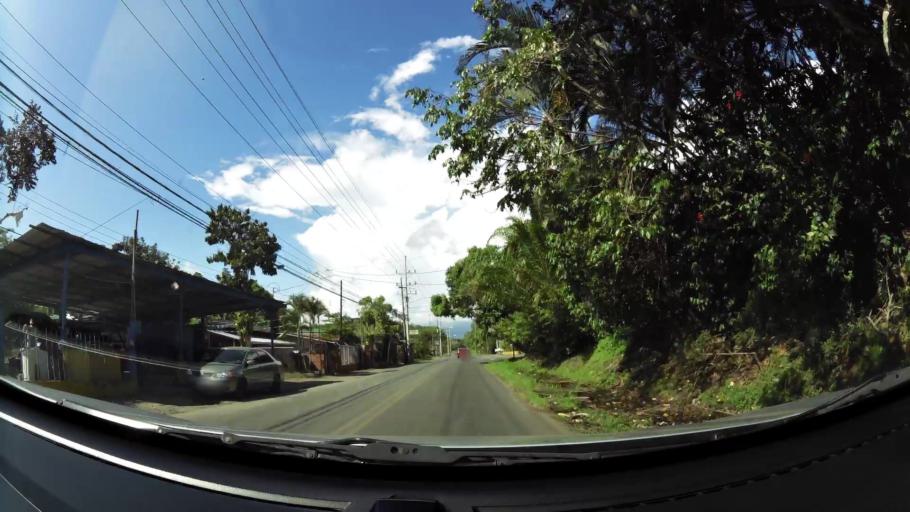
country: CR
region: Puntarenas
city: Quepos
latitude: 9.4456
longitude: -84.1659
